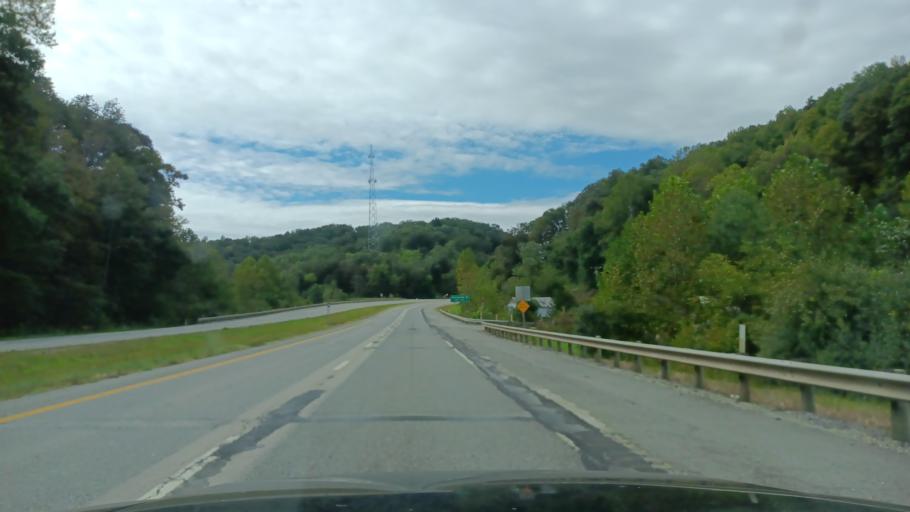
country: US
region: West Virginia
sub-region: Doddridge County
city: West Union
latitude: 39.2777
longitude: -80.8157
